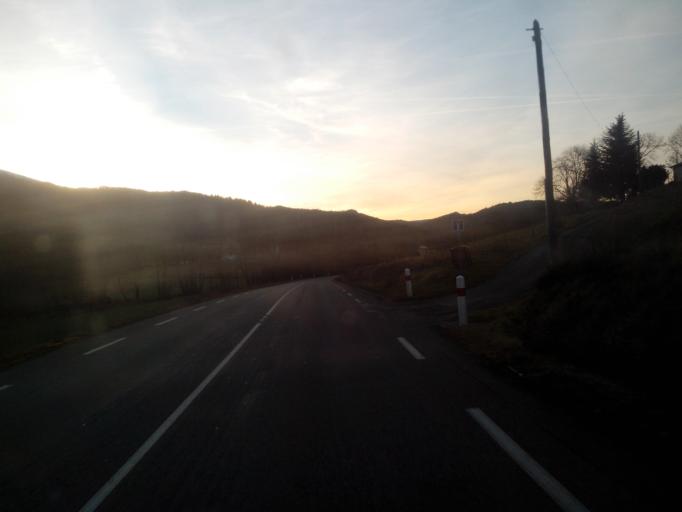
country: FR
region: Midi-Pyrenees
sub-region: Departement de l'Ariege
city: Lavelanet
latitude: 42.9158
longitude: 1.8173
